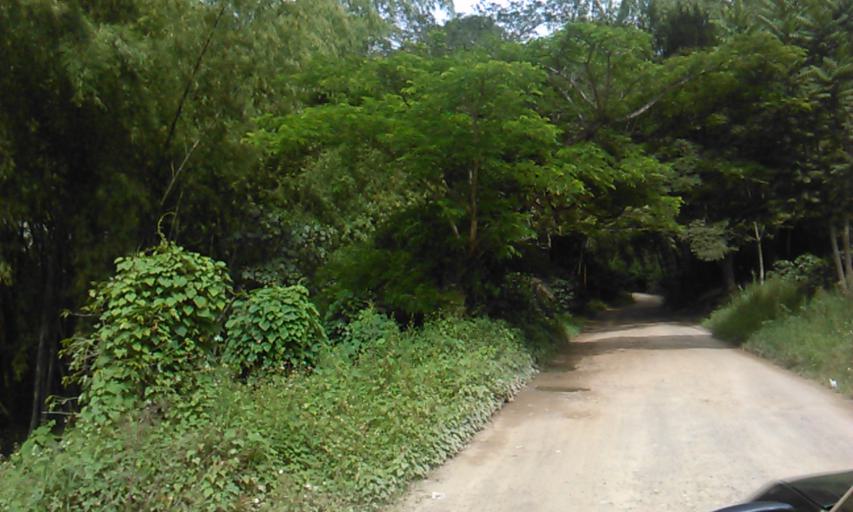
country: CO
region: Quindio
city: Cordoba
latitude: 4.4033
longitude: -75.6886
